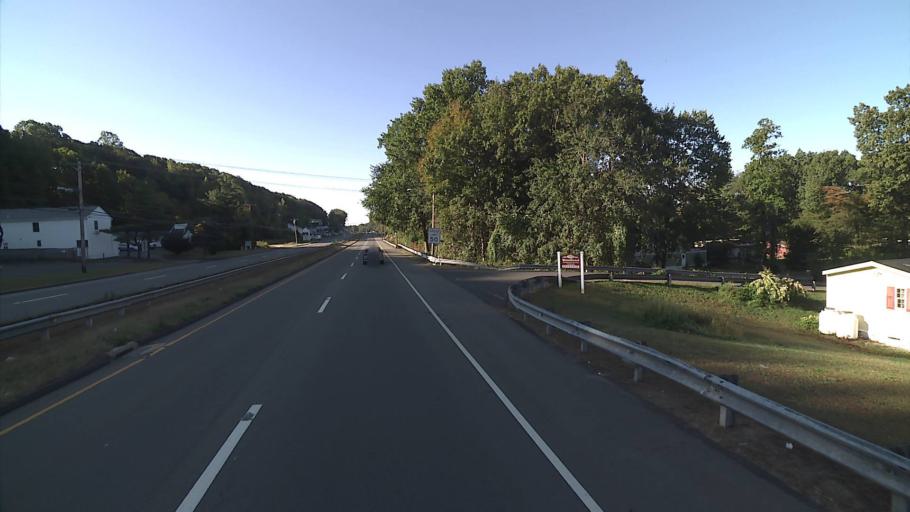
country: US
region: Connecticut
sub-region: New Haven County
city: Meriden
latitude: 41.5698
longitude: -72.7721
